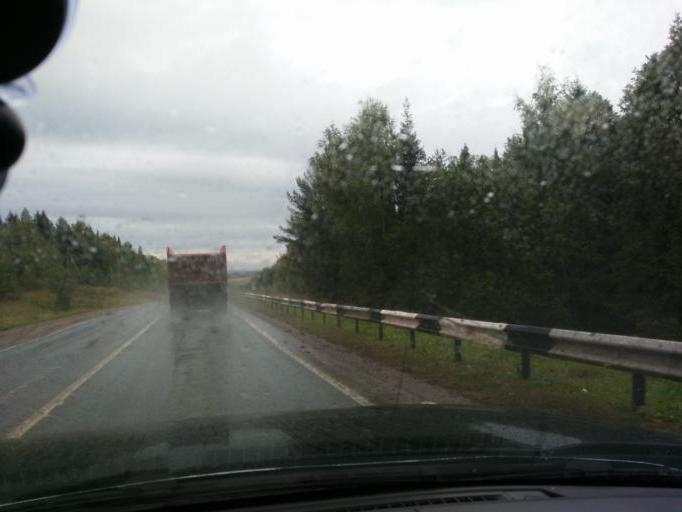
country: RU
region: Perm
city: Kultayevo
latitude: 57.8435
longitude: 55.8288
